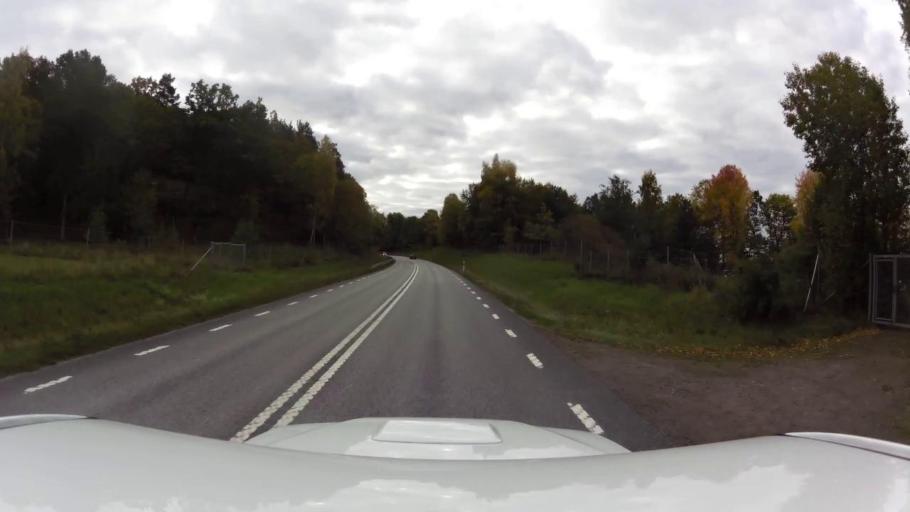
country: SE
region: OEstergoetland
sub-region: Kinda Kommun
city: Rimforsa
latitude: 58.1864
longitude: 15.6676
